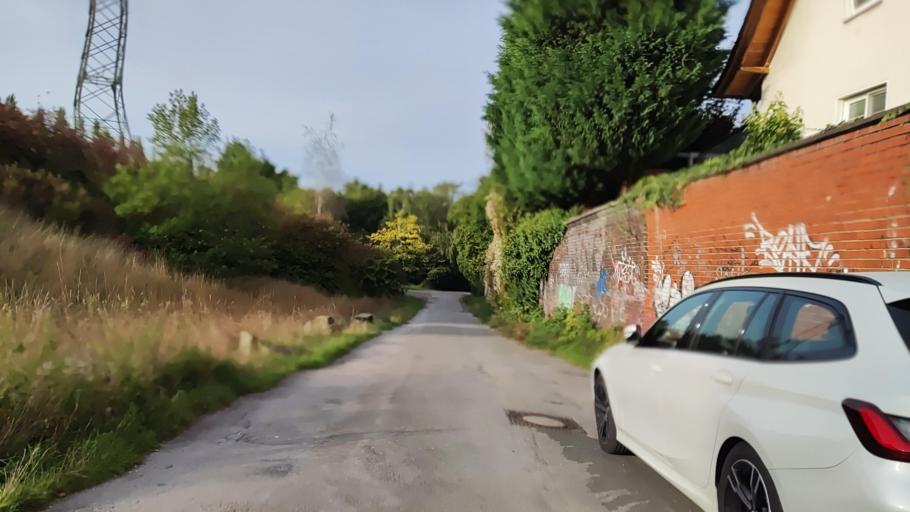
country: DE
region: North Rhine-Westphalia
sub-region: Regierungsbezirk Arnsberg
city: Herne
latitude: 51.5444
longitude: 7.2537
